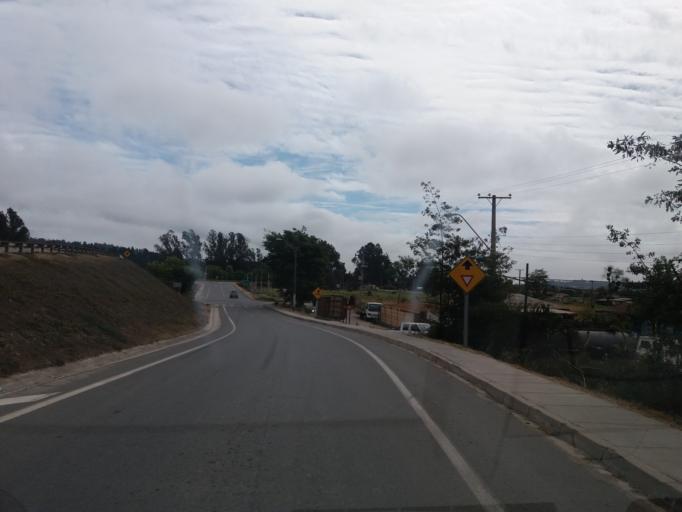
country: CL
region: Valparaiso
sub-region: Provincia de Marga Marga
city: Quilpue
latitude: -32.9311
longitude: -71.4362
